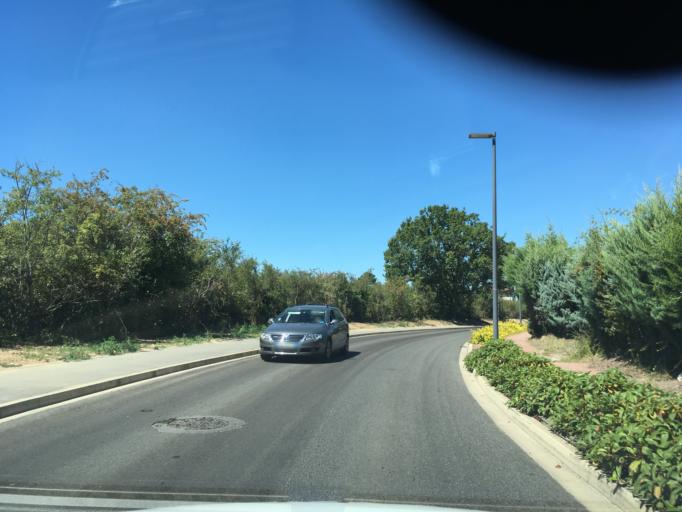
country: FR
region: Midi-Pyrenees
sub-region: Departement du Tarn-et-Garonne
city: Montauban
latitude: 44.0314
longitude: 1.3424
